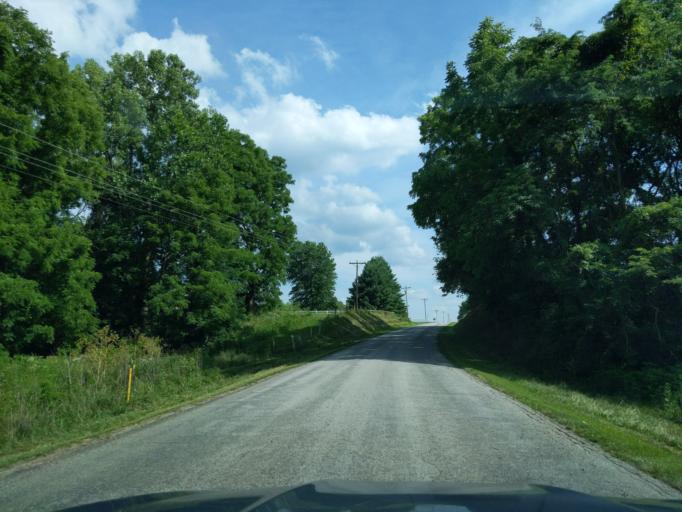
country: US
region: Indiana
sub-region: Decatur County
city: Greensburg
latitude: 39.2881
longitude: -85.4670
